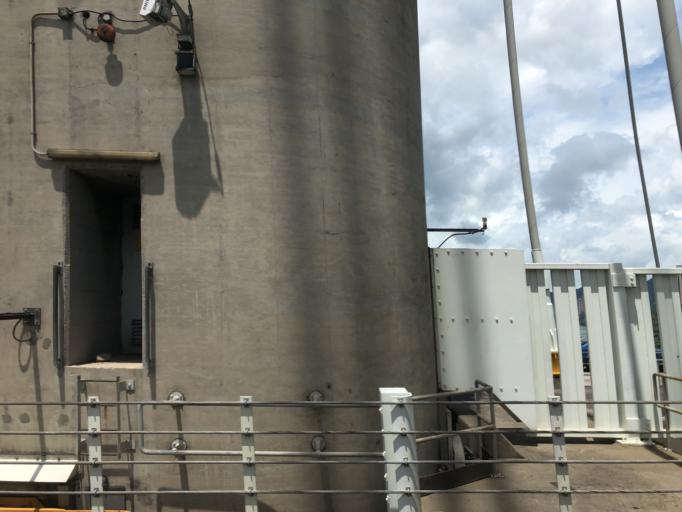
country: HK
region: Tsuen Wan
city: Tsuen Wan
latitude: 22.3643
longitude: 114.0797
